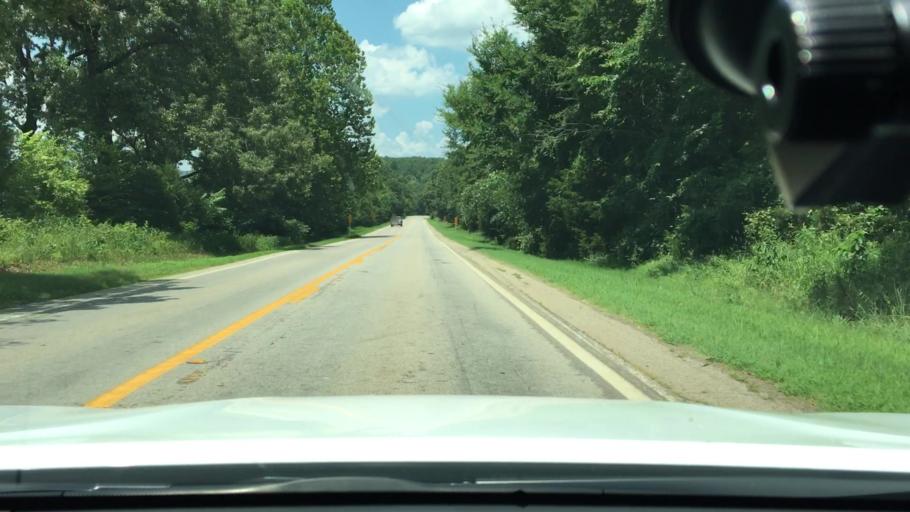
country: US
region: Arkansas
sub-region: Logan County
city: Booneville
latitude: 35.2125
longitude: -93.9344
